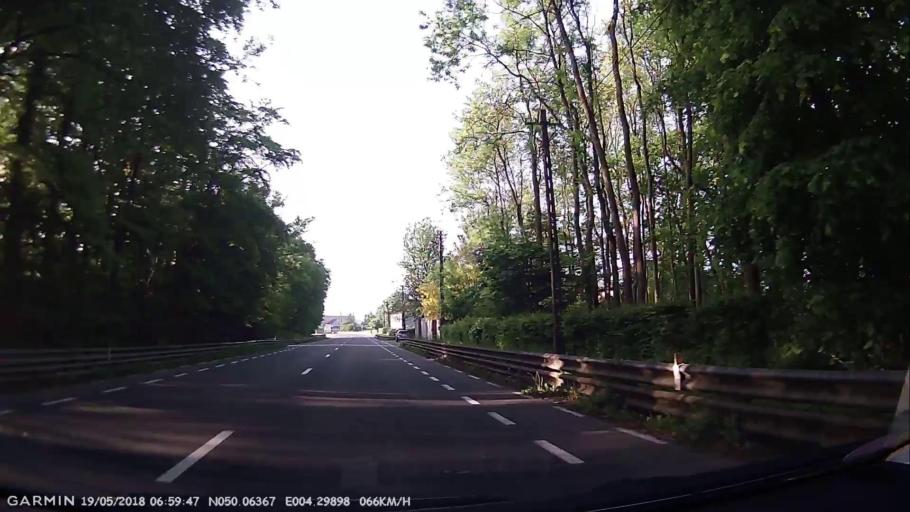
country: BE
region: Wallonia
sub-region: Province du Hainaut
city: Chimay
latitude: 50.0635
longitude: 4.2991
